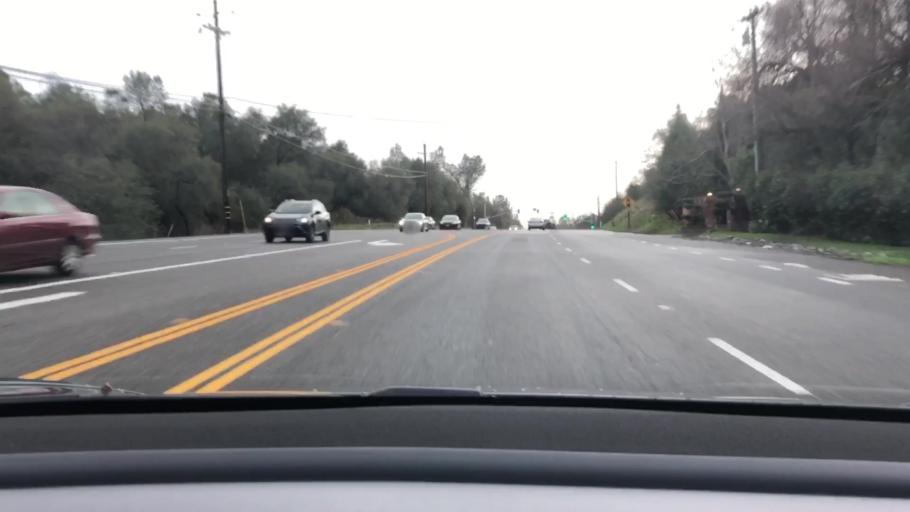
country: US
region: California
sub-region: Placer County
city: Granite Bay
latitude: 38.7215
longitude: -121.1752
